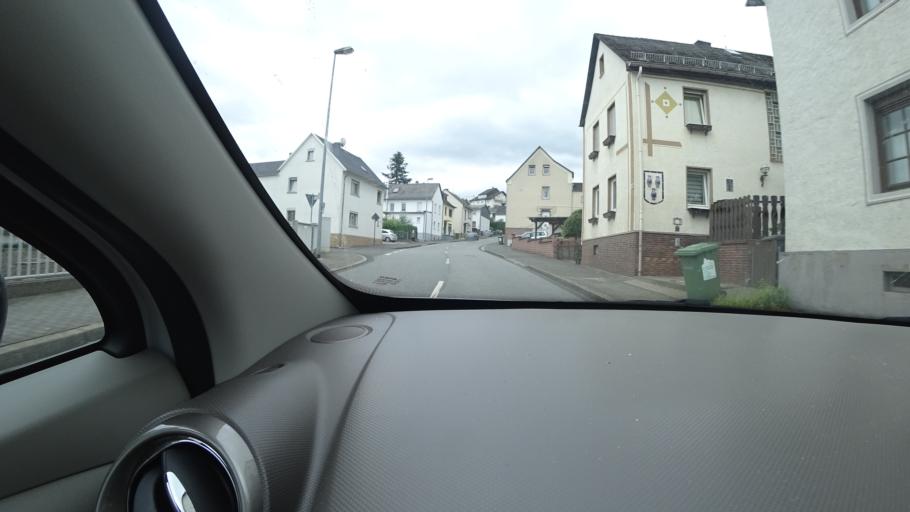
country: DE
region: Rheinland-Pfalz
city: Hohr-Grenzhausen
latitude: 50.4304
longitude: 7.6748
